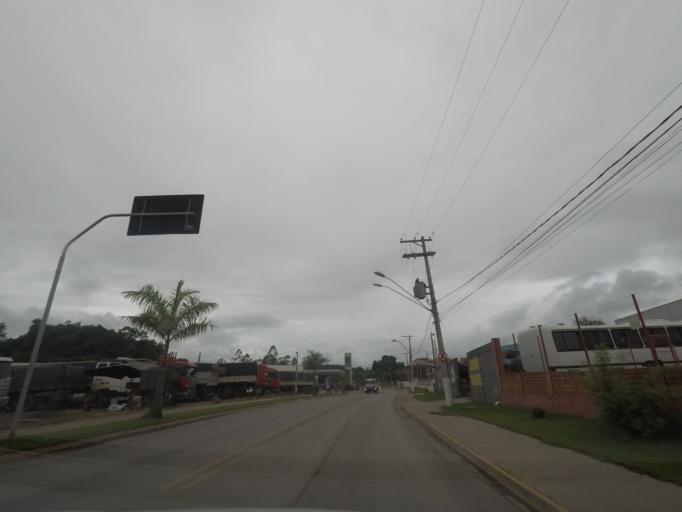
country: BR
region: Sao Paulo
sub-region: Cajati
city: Cajati
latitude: -24.7212
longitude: -48.0997
